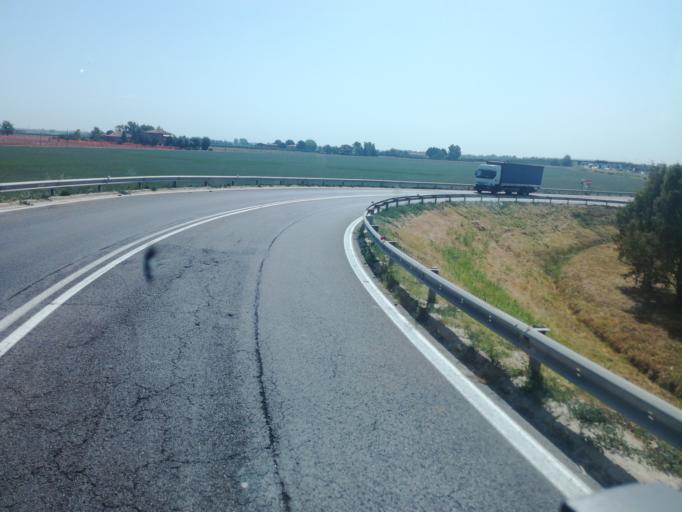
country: IT
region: Emilia-Romagna
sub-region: Provincia di Bologna
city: Castel San Pietro Terme
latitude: 44.4268
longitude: 11.6093
